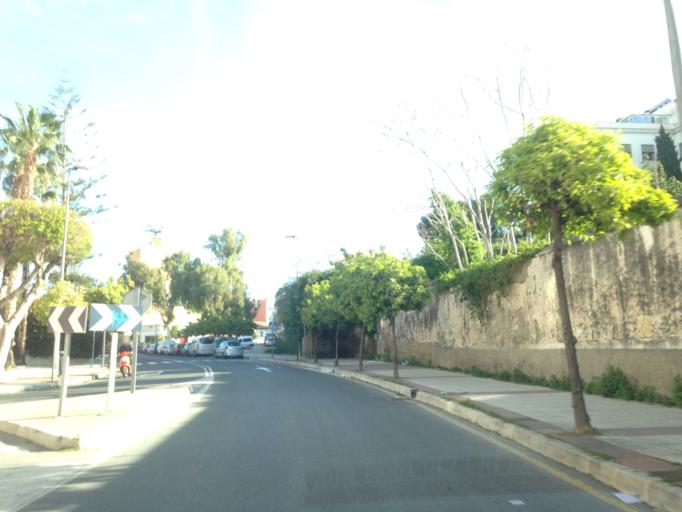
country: ES
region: Andalusia
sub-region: Provincia de Malaga
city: Malaga
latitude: 36.7327
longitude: -4.4240
